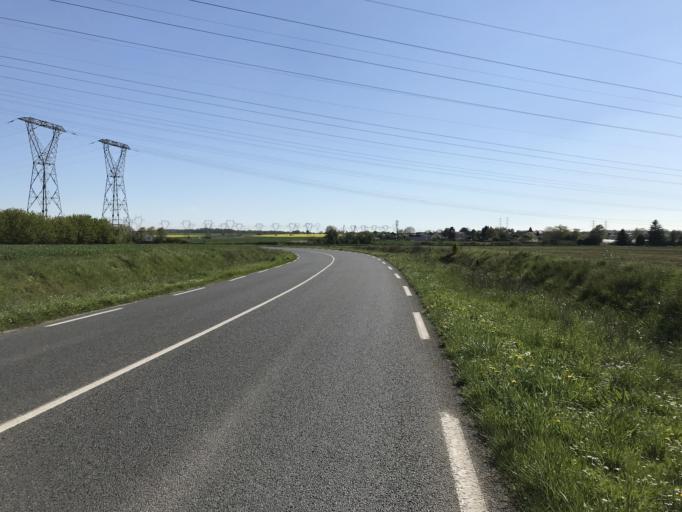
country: FR
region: Ile-de-France
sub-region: Departement de l'Essonne
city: Villejust
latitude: 48.6792
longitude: 2.2257
